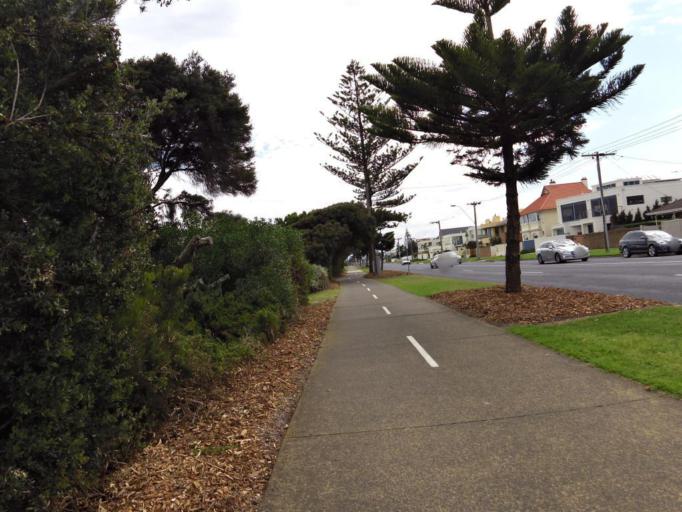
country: AU
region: Victoria
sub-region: Bayside
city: Hampton
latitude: -37.9376
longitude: 144.9981
